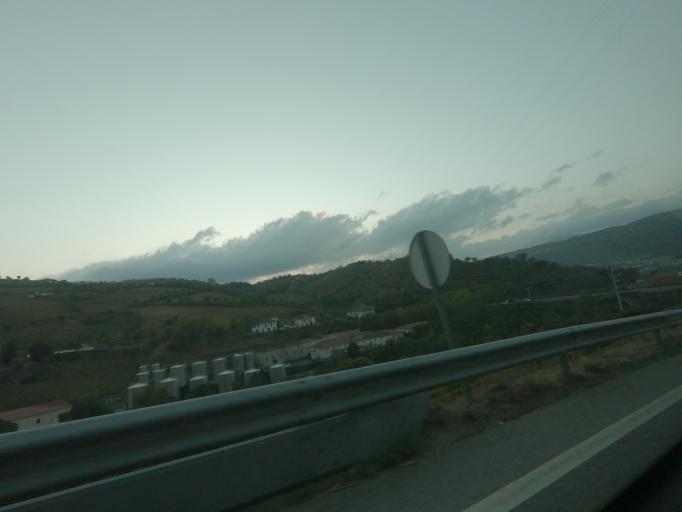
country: PT
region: Vila Real
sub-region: Peso da Regua
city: Peso da Regua
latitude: 41.1504
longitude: -7.7804
